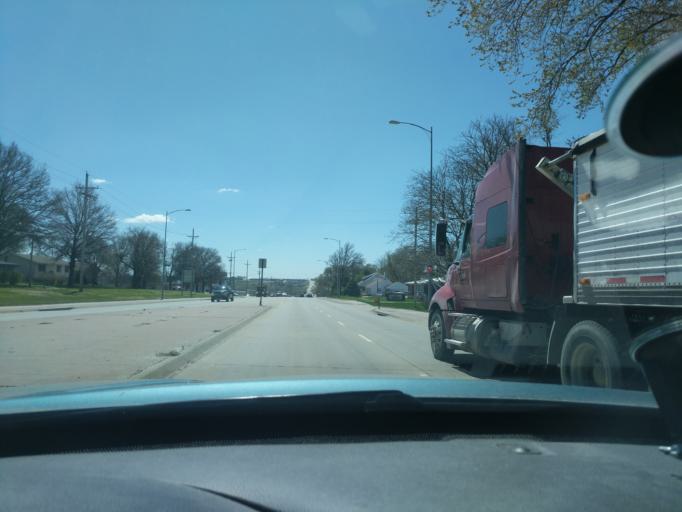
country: US
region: Nebraska
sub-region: Douglas County
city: Elkhorn
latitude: 41.2904
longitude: -96.2344
